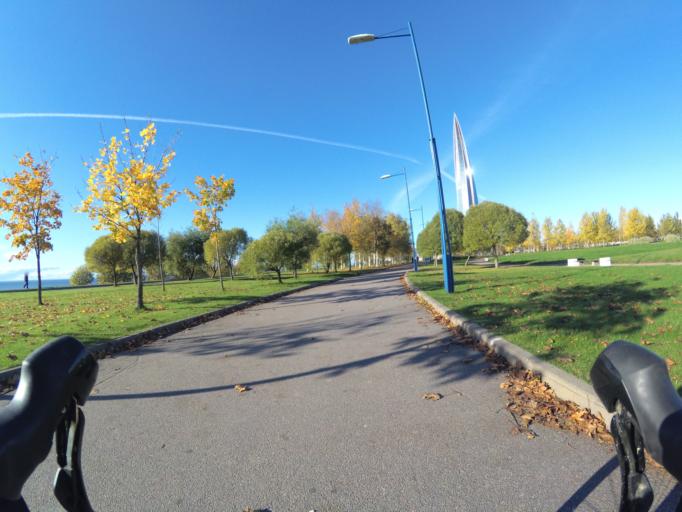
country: RU
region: Leningrad
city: Untolovo
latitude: 59.9829
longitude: 30.1926
